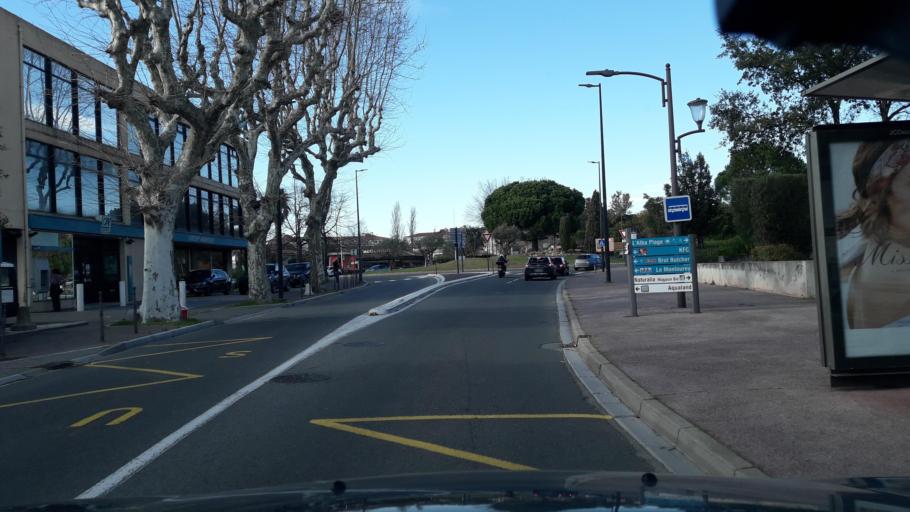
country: FR
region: Provence-Alpes-Cote d'Azur
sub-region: Departement du Var
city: Frejus
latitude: 43.4271
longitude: 6.7372
